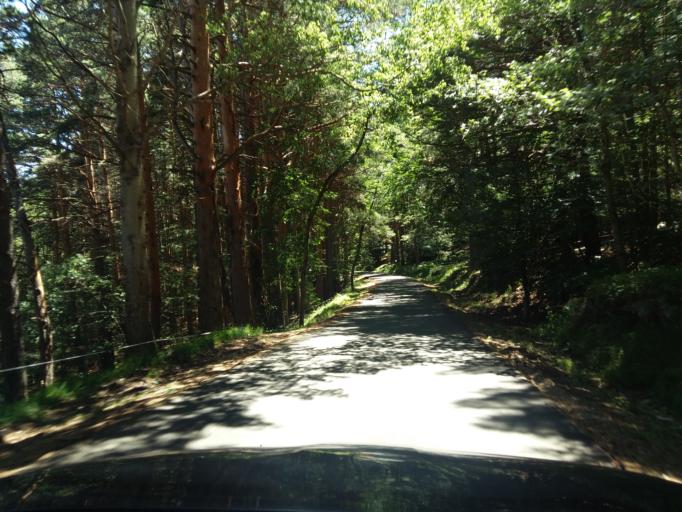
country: ES
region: Castille and Leon
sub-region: Provincia de Soria
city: Vozmediano
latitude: 41.8109
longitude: -1.8145
